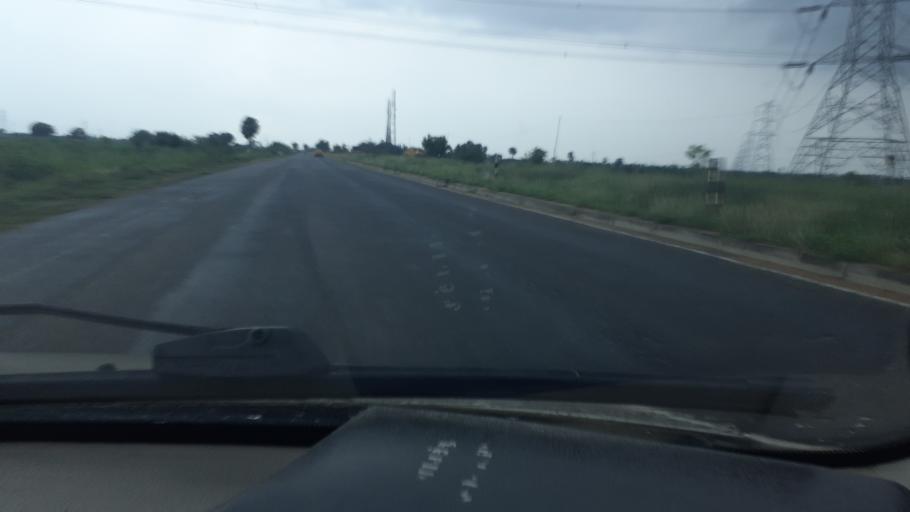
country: IN
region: Tamil Nadu
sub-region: Thoothukkudi
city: Kadambur
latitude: 9.0692
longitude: 77.7992
